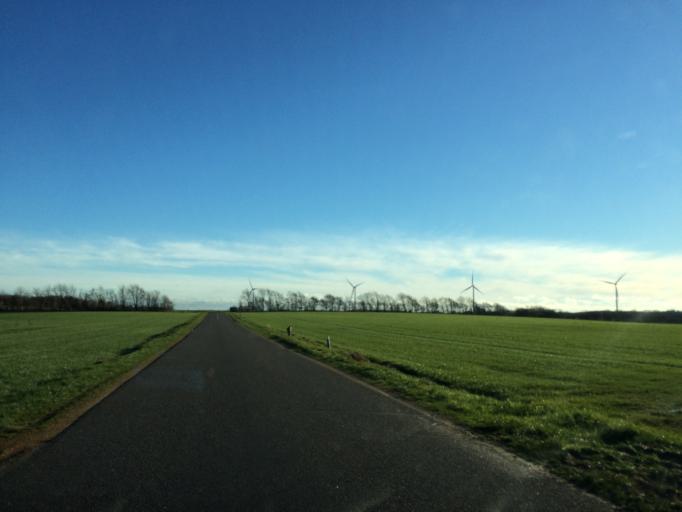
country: DK
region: Central Jutland
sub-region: Ringkobing-Skjern Kommune
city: Videbaek
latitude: 56.1286
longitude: 8.6107
